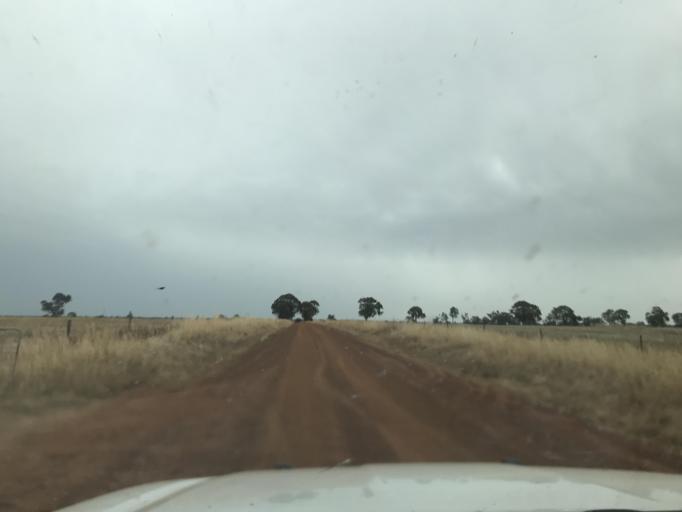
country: AU
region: Victoria
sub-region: Horsham
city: Horsham
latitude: -37.0616
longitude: 141.6210
